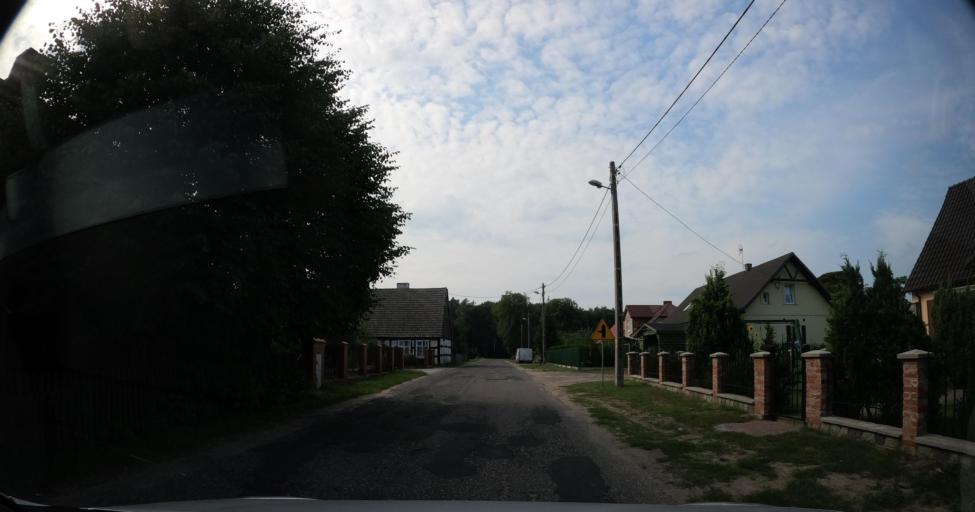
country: PL
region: West Pomeranian Voivodeship
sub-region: Powiat goleniowski
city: Goleniow
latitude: 53.5065
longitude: 14.8689
